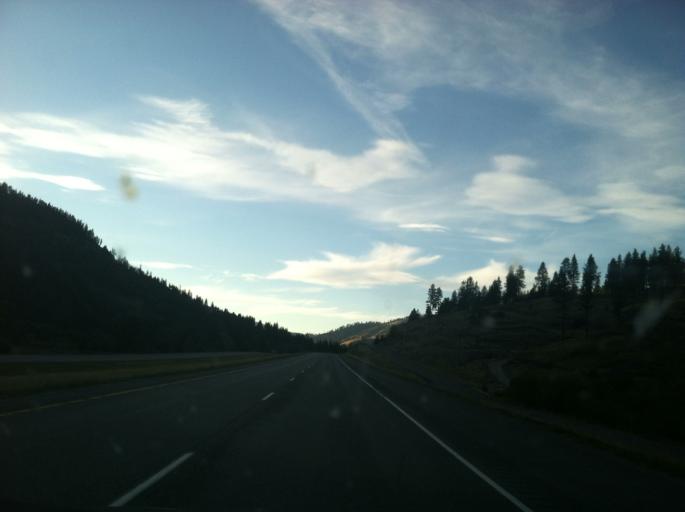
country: US
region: Montana
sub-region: Missoula County
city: Clinton
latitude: 46.7021
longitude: -113.4973
